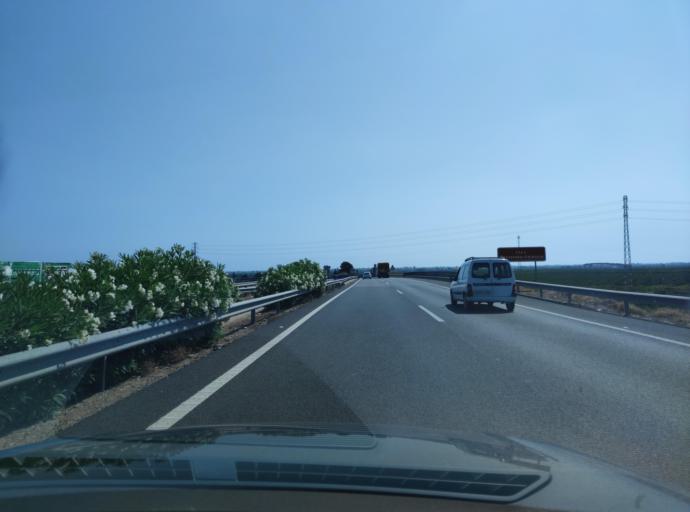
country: ES
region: Valencia
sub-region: Provincia de Valencia
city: Faura
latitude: 39.7041
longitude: -0.2516
